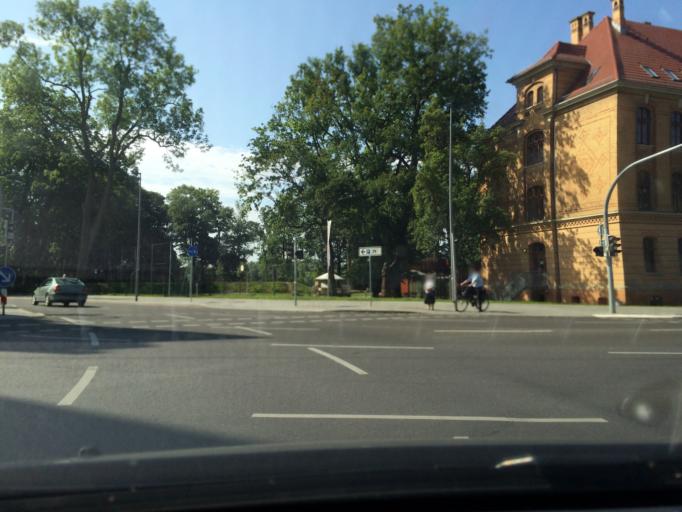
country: DE
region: Mecklenburg-Vorpommern
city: Stralsund
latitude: 54.3094
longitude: 13.0839
